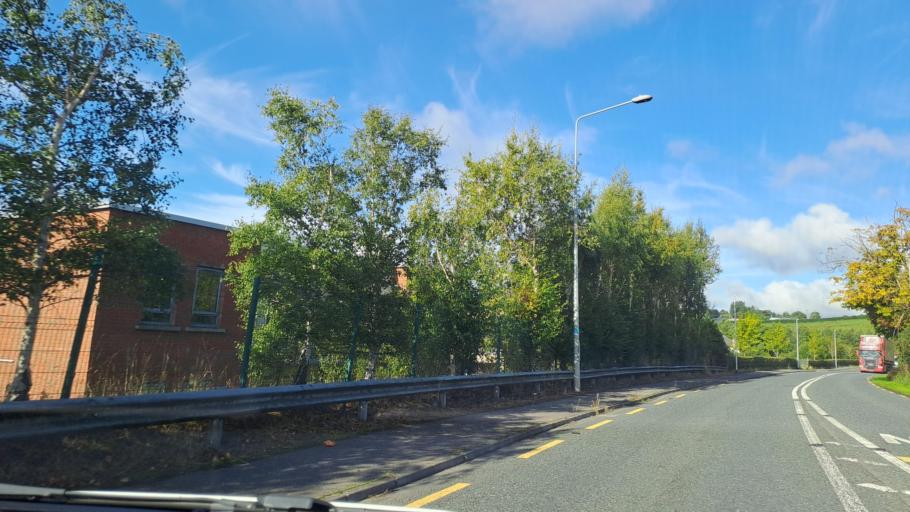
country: IE
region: Ulster
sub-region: County Monaghan
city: Carrickmacross
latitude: 53.9719
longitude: -6.7262
